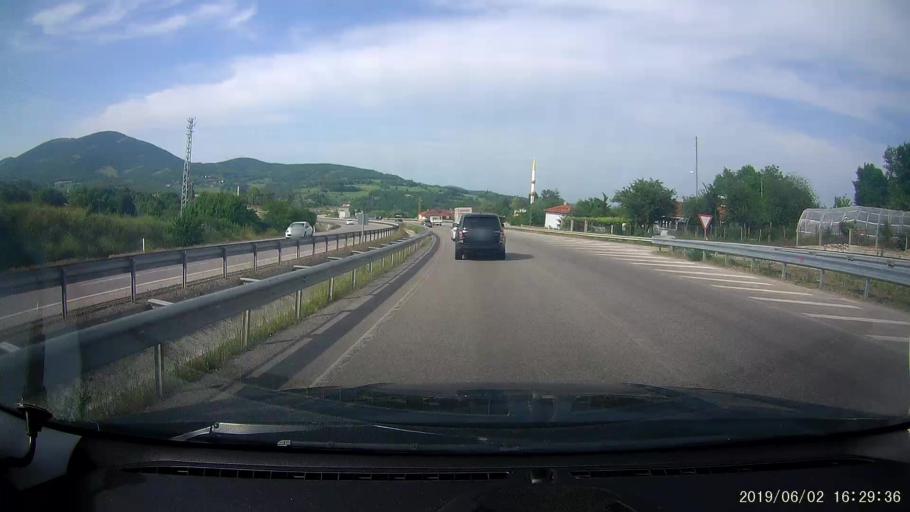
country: TR
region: Samsun
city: Ladik
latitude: 41.0147
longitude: 35.8714
